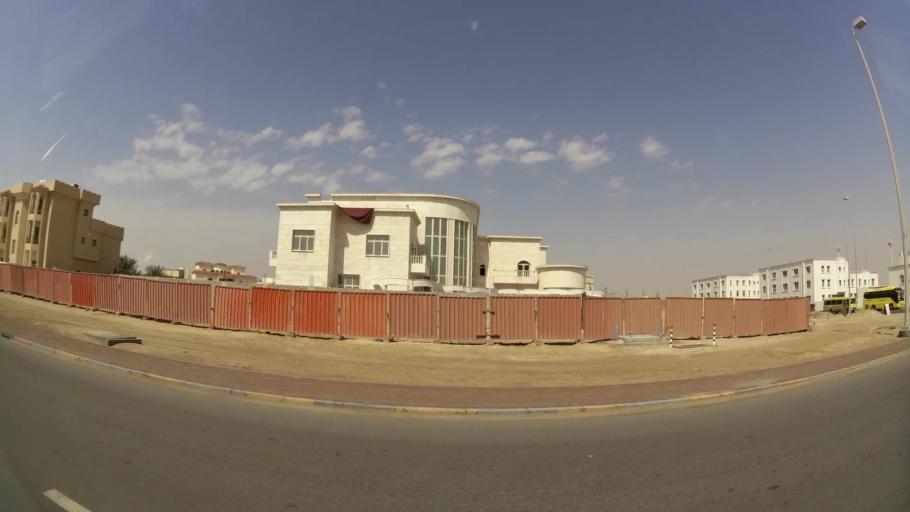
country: AE
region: Abu Dhabi
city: Abu Dhabi
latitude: 24.3168
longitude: 54.5741
